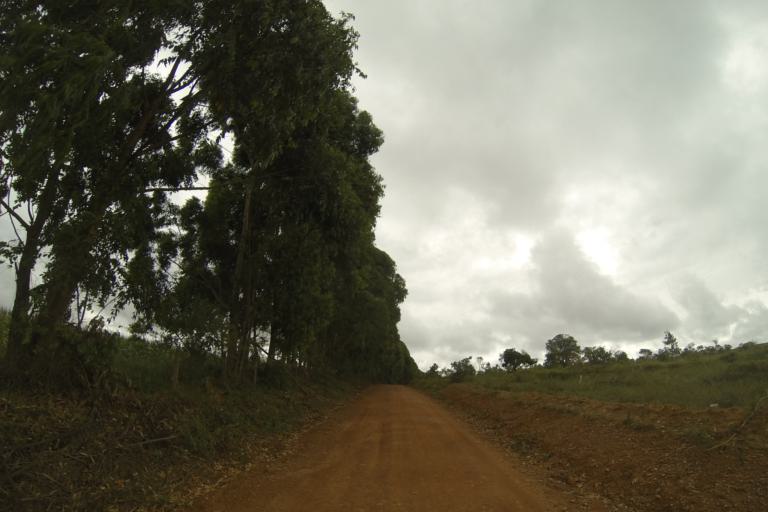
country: BR
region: Minas Gerais
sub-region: Ibia
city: Ibia
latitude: -19.7441
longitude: -46.4898
